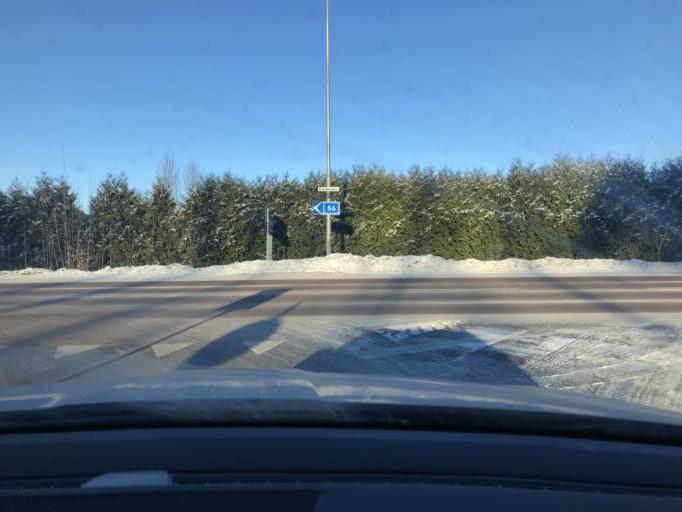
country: SE
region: Vaestmanland
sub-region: Vasteras
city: Hokasen
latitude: 59.6673
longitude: 16.5919
